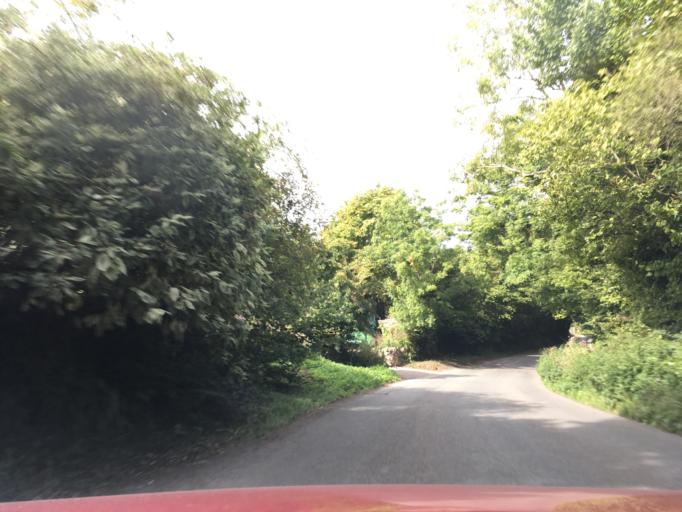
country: GB
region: England
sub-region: South Gloucestershire
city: Alveston
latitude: 51.6092
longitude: -2.5483
